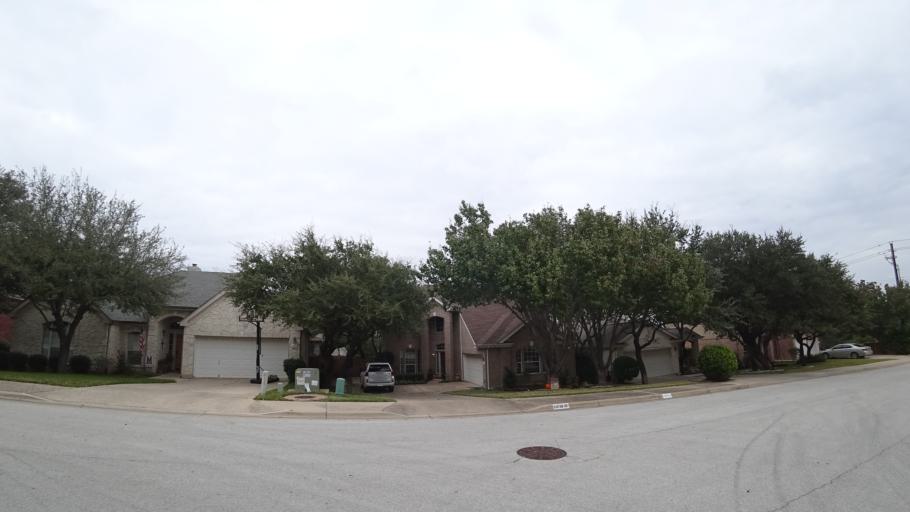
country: US
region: Texas
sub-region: Travis County
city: Bee Cave
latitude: 30.3153
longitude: -97.9163
